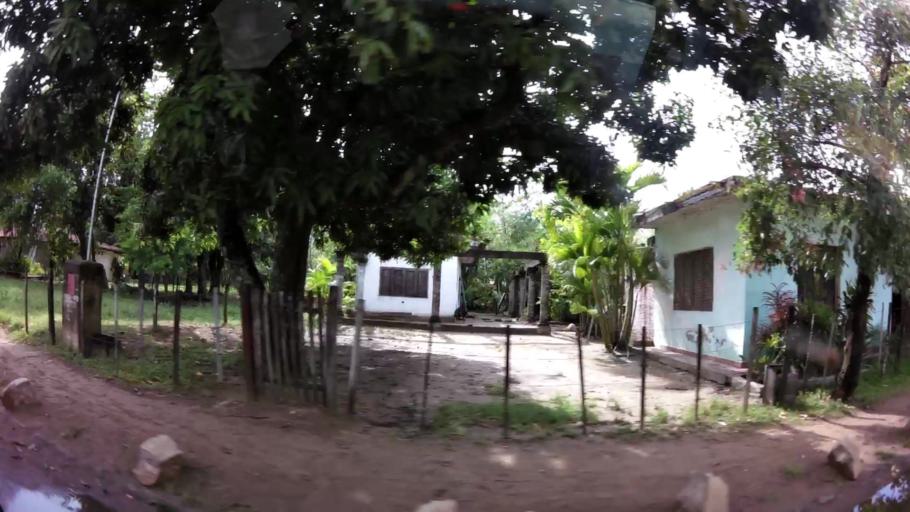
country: PY
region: Central
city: Limpio
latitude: -25.1451
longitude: -57.4728
